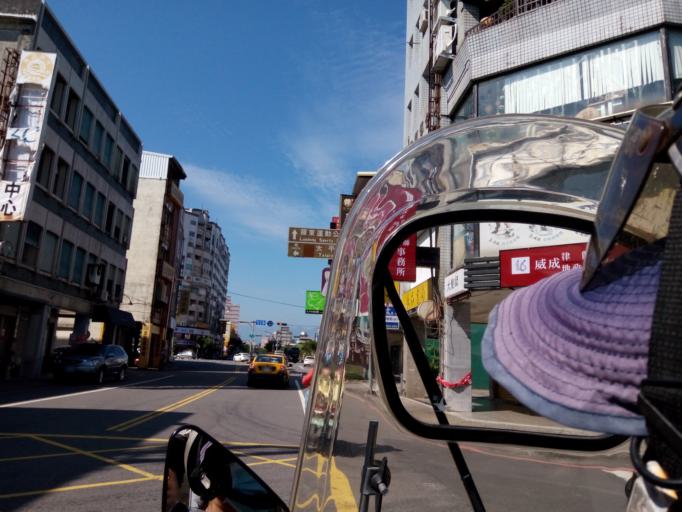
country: TW
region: Taiwan
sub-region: Yilan
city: Yilan
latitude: 24.6799
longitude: 121.7650
